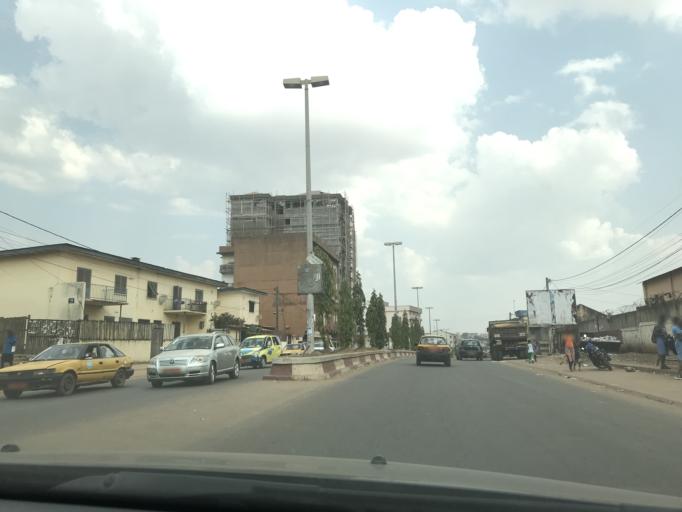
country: CM
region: Centre
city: Yaounde
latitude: 3.8888
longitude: 11.5238
